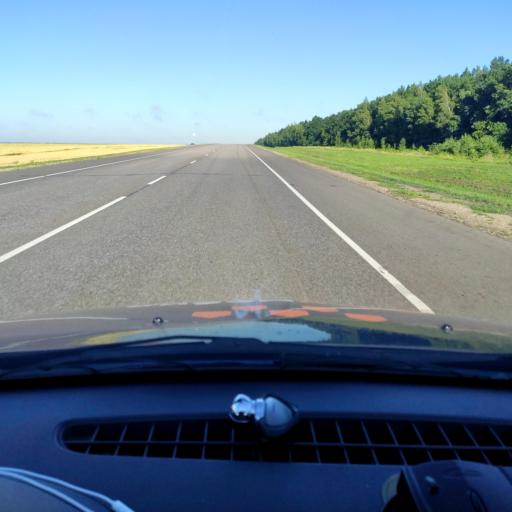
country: RU
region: Orjol
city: Pokrovskoye
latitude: 52.6233
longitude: 36.8246
